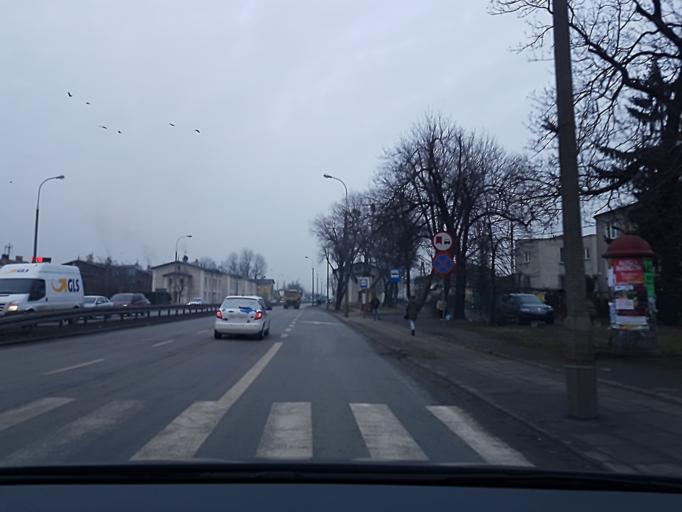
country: PL
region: Masovian Voivodeship
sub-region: Powiat wolominski
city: Marki
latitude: 52.3178
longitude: 21.1011
